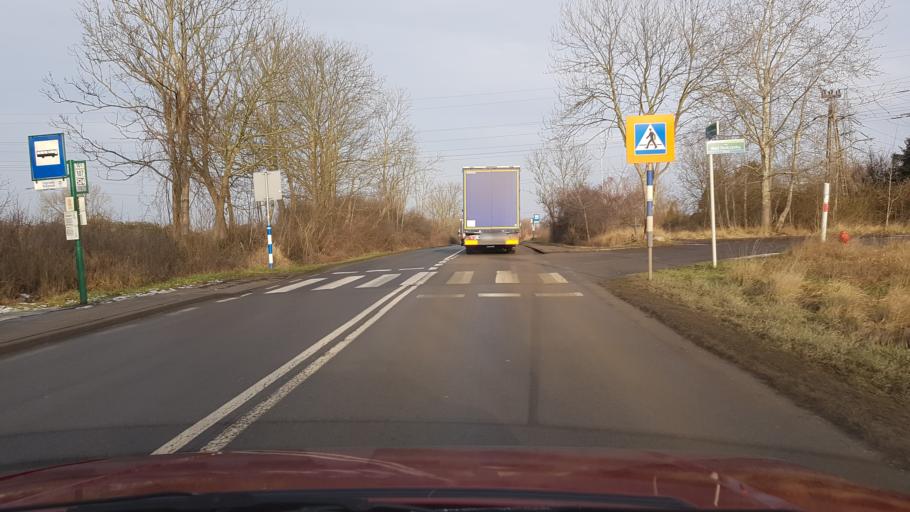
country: PL
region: West Pomeranian Voivodeship
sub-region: Powiat policki
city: Police
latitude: 53.4978
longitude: 14.5813
